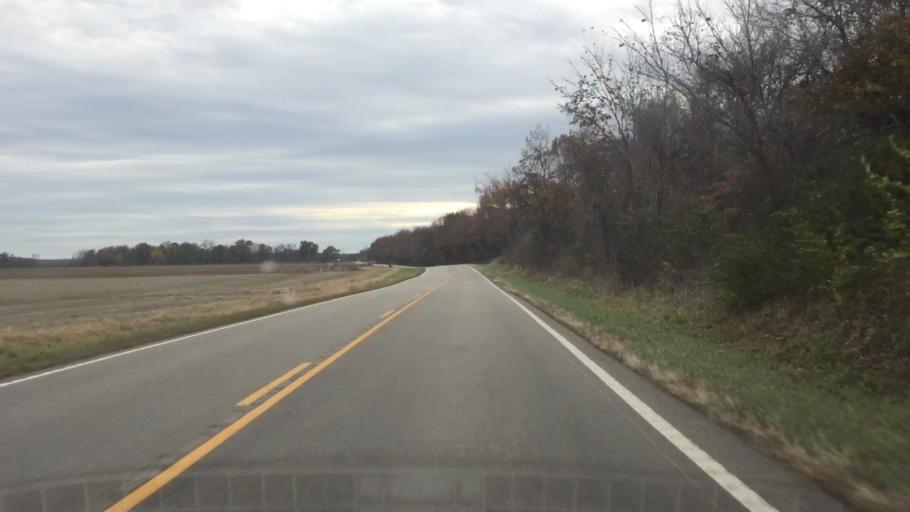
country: US
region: Missouri
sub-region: Callaway County
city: Holts Summit
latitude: 38.6086
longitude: -91.9851
